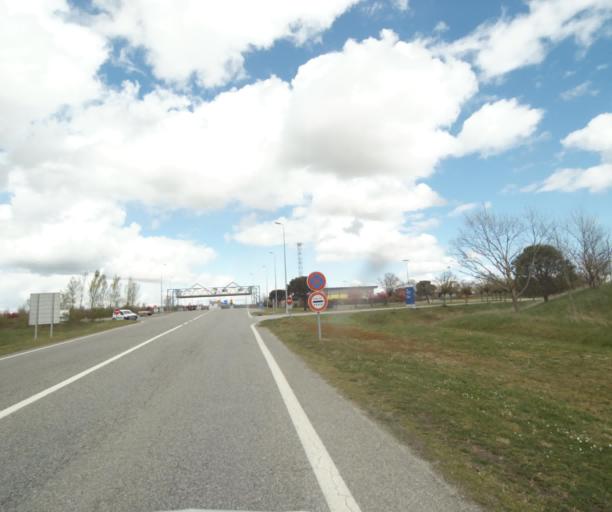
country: FR
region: Midi-Pyrenees
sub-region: Departement de l'Ariege
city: Mazeres
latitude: 43.2335
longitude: 1.6344
